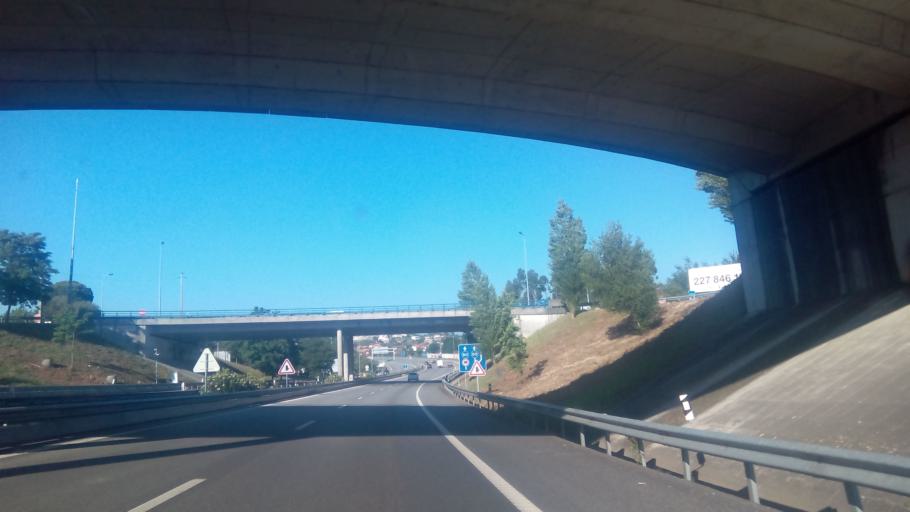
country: PT
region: Porto
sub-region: Pacos de Ferreira
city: Frazao
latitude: 41.2568
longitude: -8.3997
